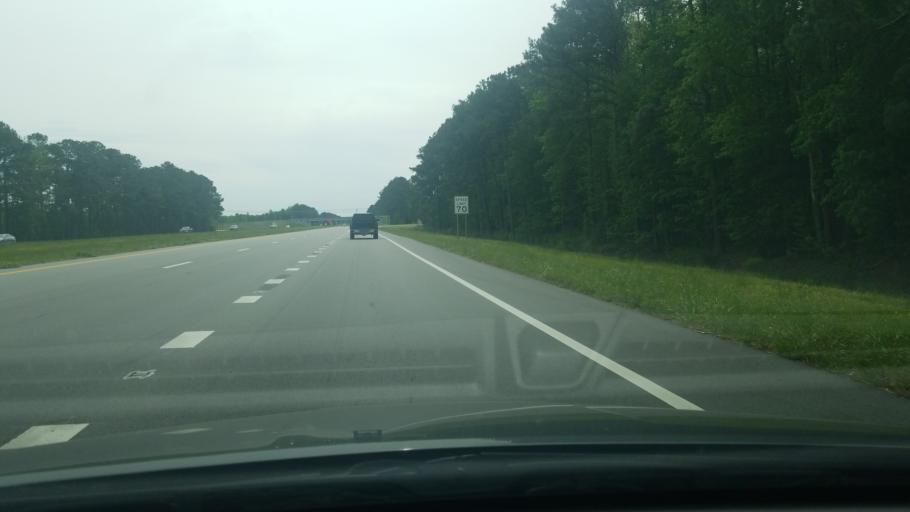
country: US
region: North Carolina
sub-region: Craven County
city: River Bend
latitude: 35.1290
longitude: -77.1413
